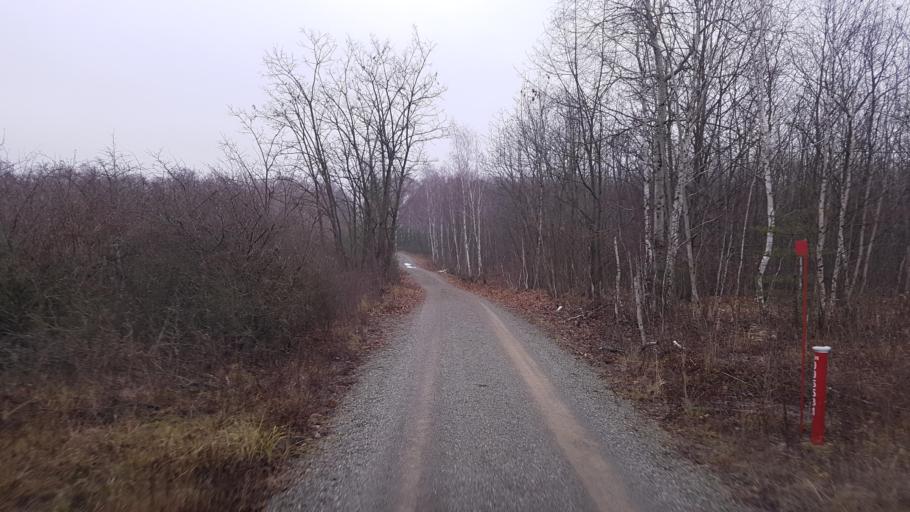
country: DE
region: Brandenburg
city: Plessa
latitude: 51.4883
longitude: 13.6390
